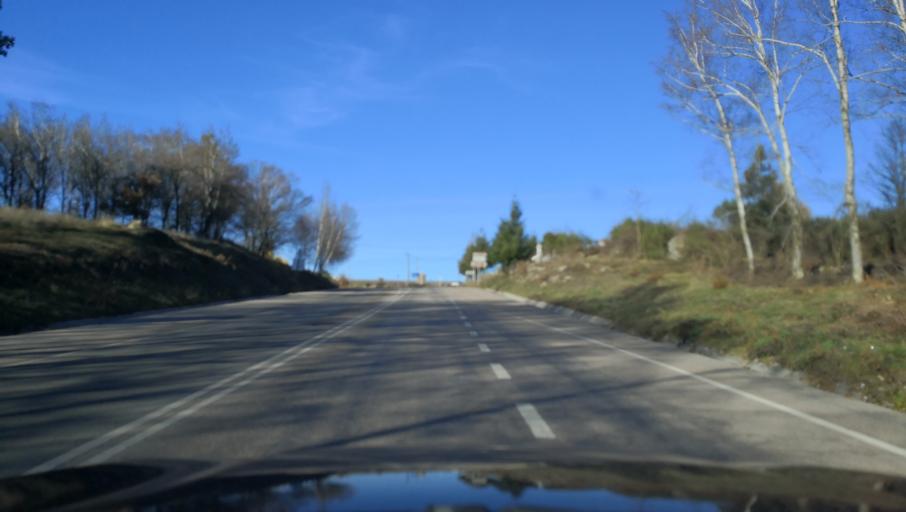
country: PT
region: Vila Real
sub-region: Vila Pouca de Aguiar
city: Vila Pouca de Aguiar
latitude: 41.4919
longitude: -7.6692
